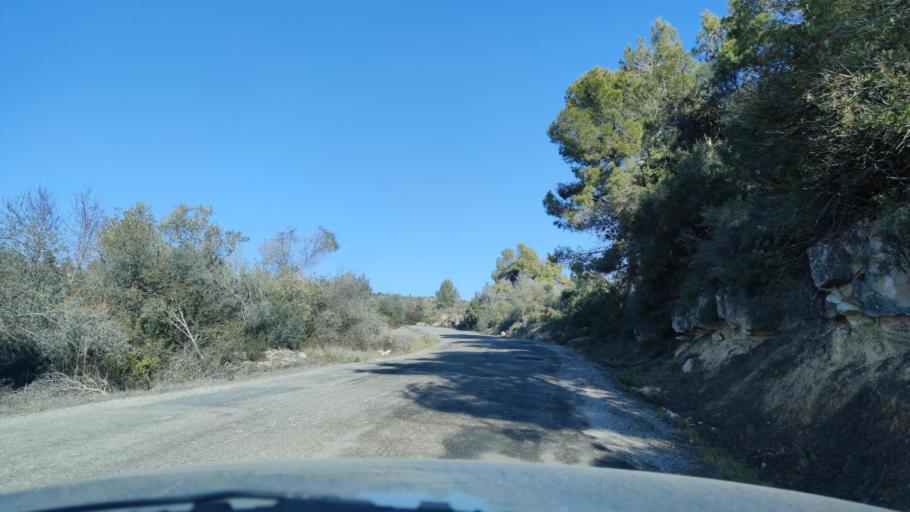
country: ES
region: Catalonia
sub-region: Provincia de Lleida
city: Torrebesses
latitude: 41.4015
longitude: 0.5654
